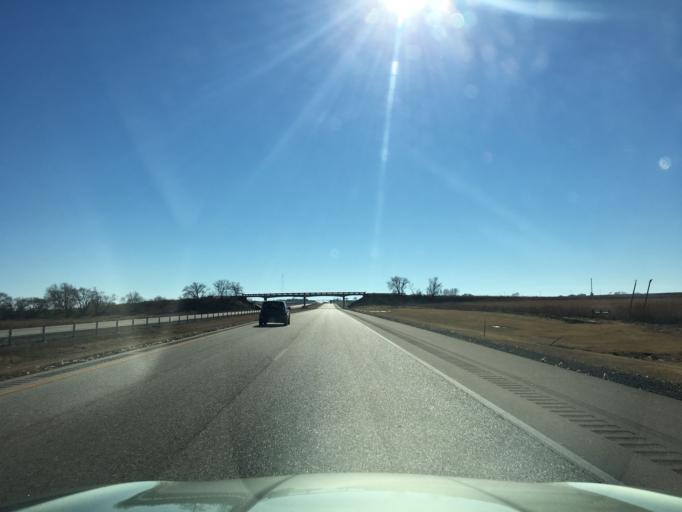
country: US
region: Oklahoma
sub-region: Kay County
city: Blackwell
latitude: 36.8863
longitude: -97.3525
